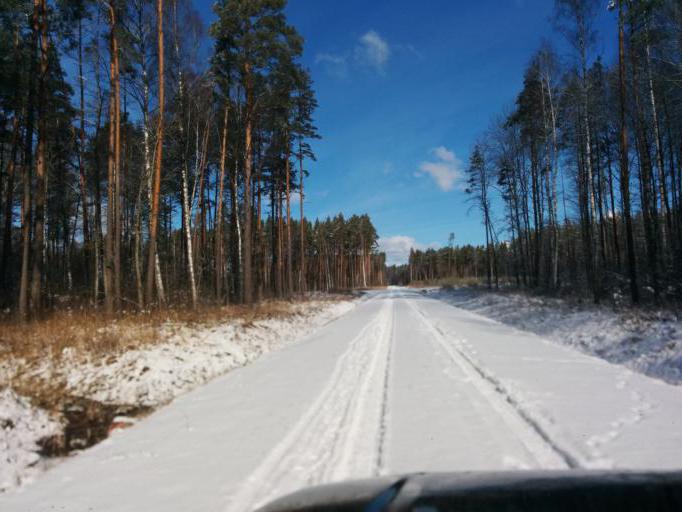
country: LV
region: Jelgava
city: Jelgava
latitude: 56.6186
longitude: 23.6682
